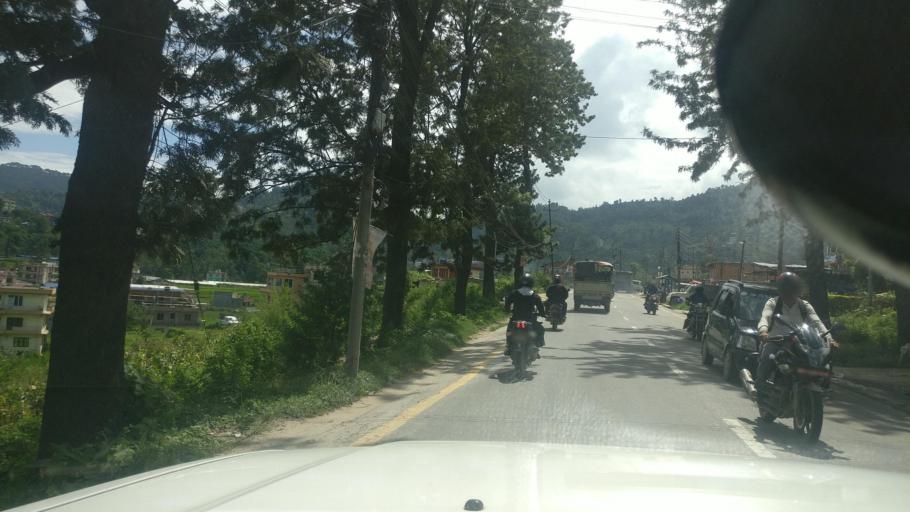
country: NP
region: Central Region
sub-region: Bagmati Zone
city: Hari Bdr Tamang House
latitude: 27.6523
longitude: 85.4613
